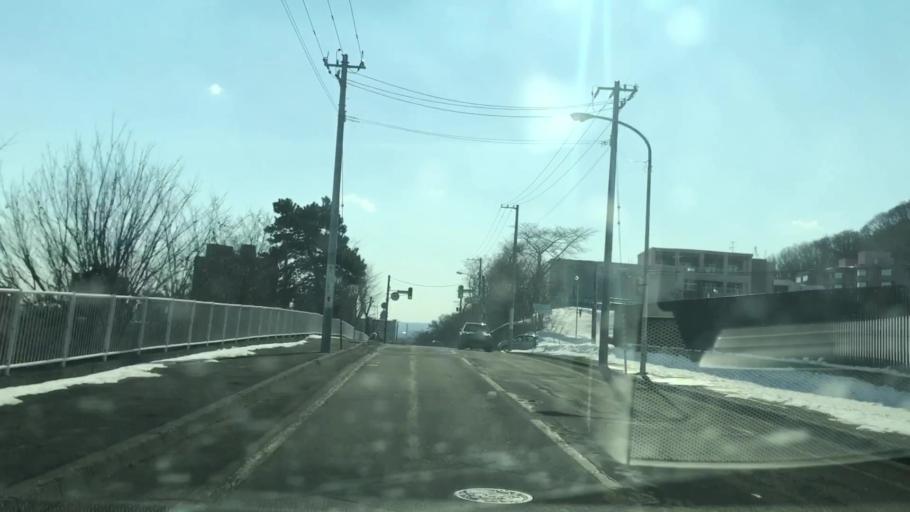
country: JP
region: Hokkaido
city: Sapporo
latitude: 43.0350
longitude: 141.3306
